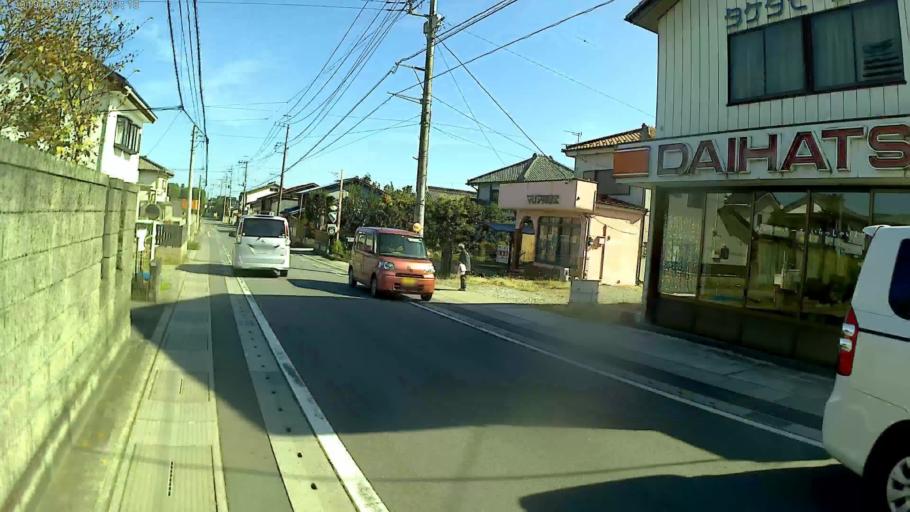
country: JP
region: Gunma
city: Annaka
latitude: 36.3155
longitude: 138.8649
